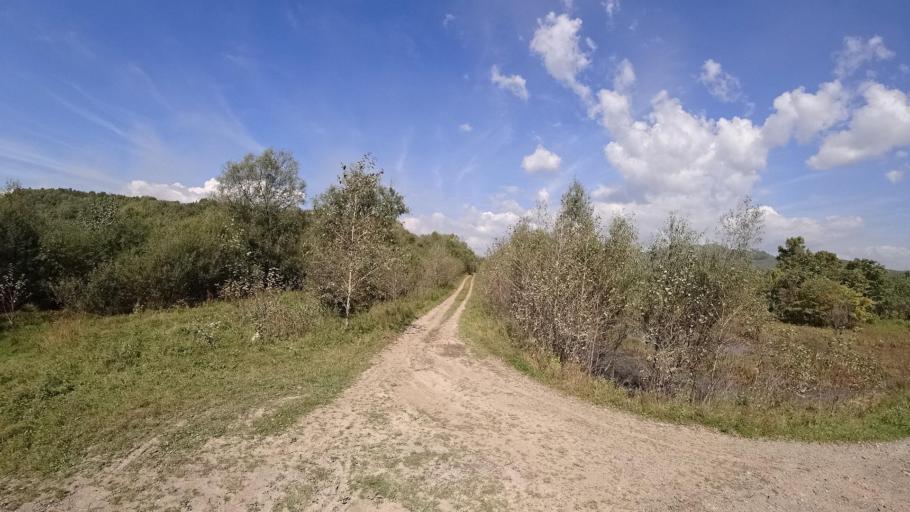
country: RU
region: Jewish Autonomous Oblast
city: Londoko
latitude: 49.0032
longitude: 131.9384
